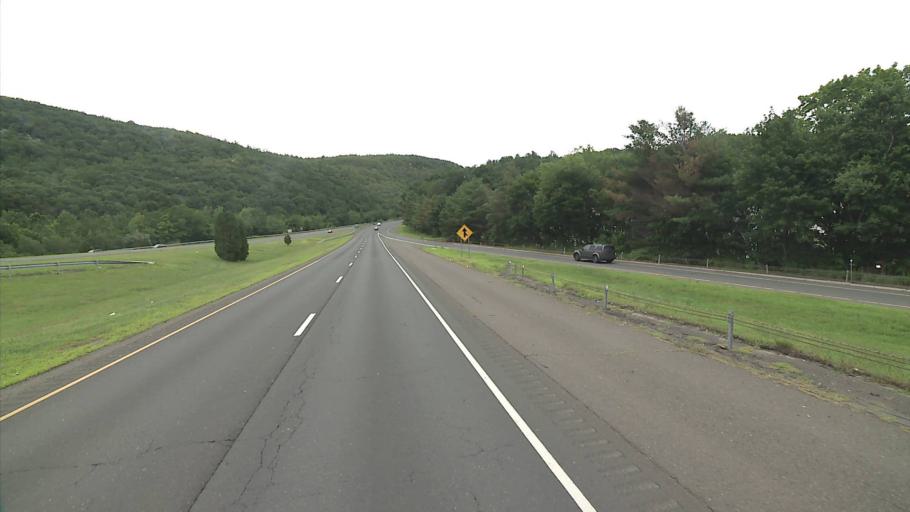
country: US
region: Connecticut
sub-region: New Haven County
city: Naugatuck
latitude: 41.4453
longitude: -73.0669
